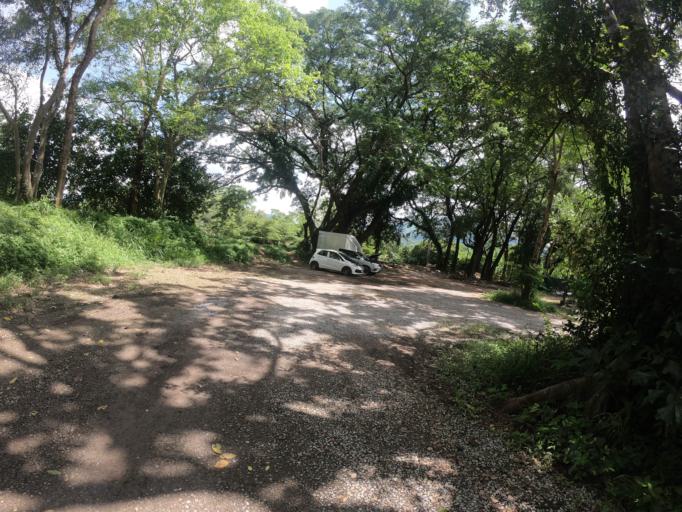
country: TH
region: Nakhon Nayok
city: Nakhon Nayok
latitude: 14.3109
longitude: 101.3129
